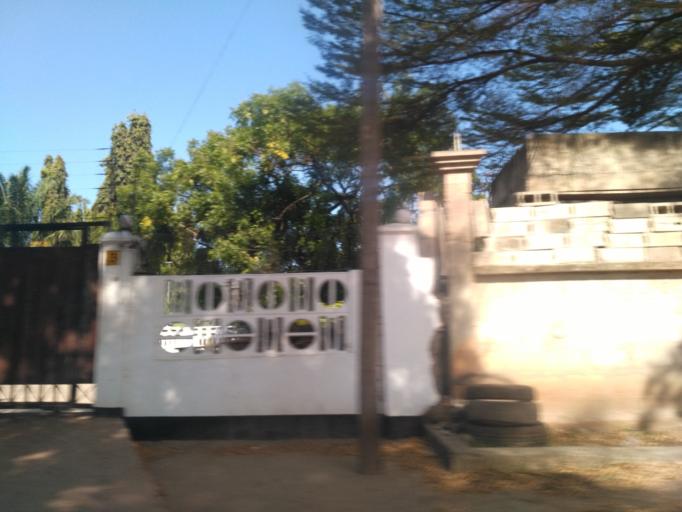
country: TZ
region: Dar es Salaam
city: Magomeni
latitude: -6.7795
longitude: 39.2680
